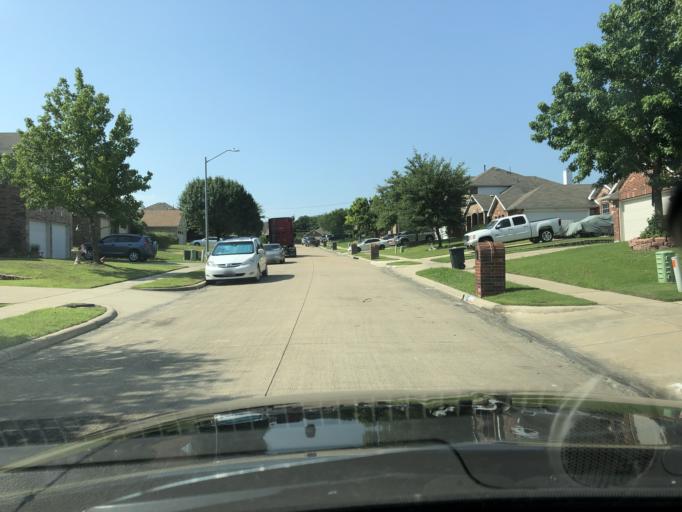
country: US
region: Texas
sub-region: Dallas County
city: Sunnyvale
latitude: 32.8263
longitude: -96.5966
